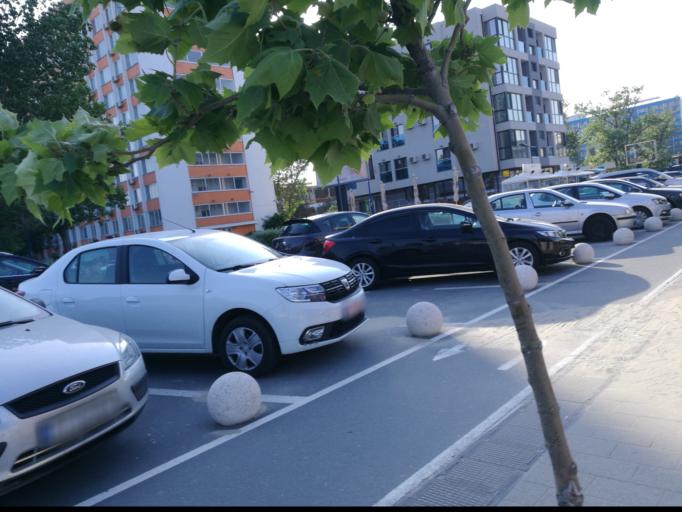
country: RO
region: Constanta
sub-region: Municipiul Constanta
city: Palazu Mare
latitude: 44.2251
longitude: 28.6314
